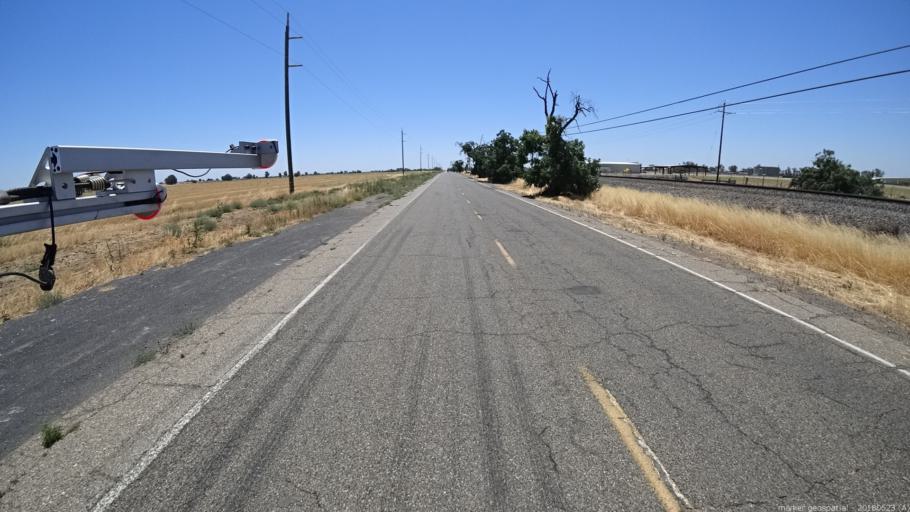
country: US
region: California
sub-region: Madera County
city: Chowchilla
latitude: 37.1133
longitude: -120.2427
